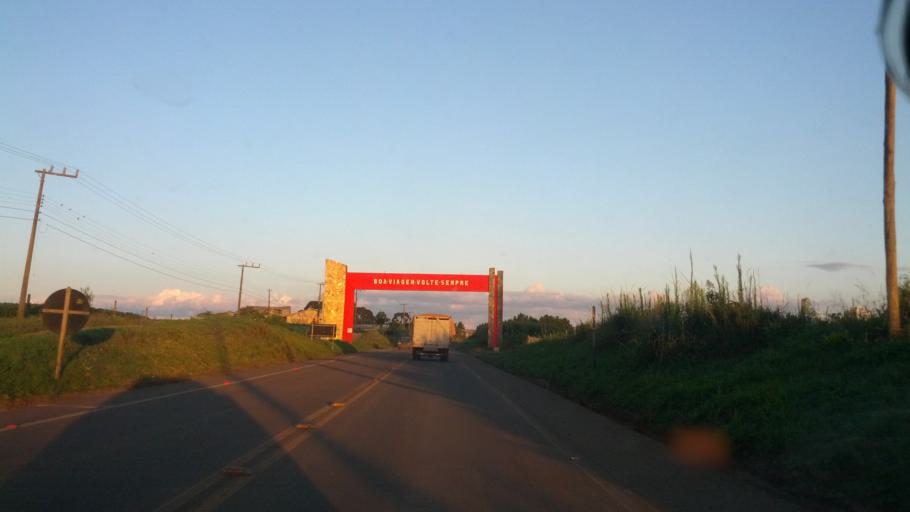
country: BR
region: Rio Grande do Sul
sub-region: Vacaria
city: Estrela
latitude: -27.7970
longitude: -50.8664
